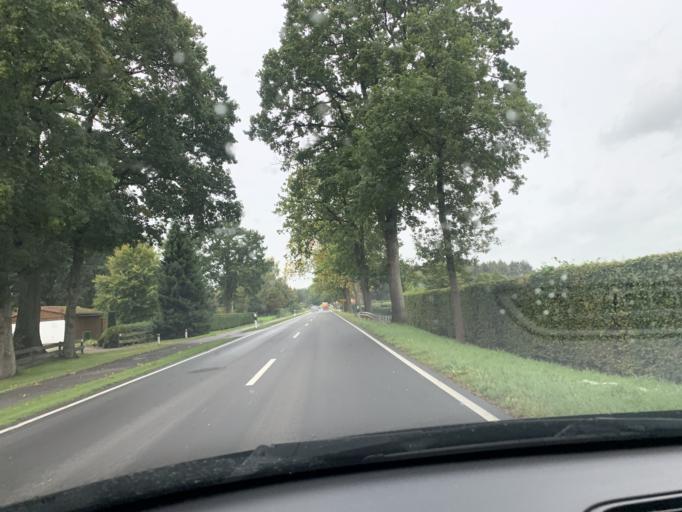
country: DE
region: Lower Saxony
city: Bad Zwischenahn
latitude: 53.1647
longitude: 8.0714
